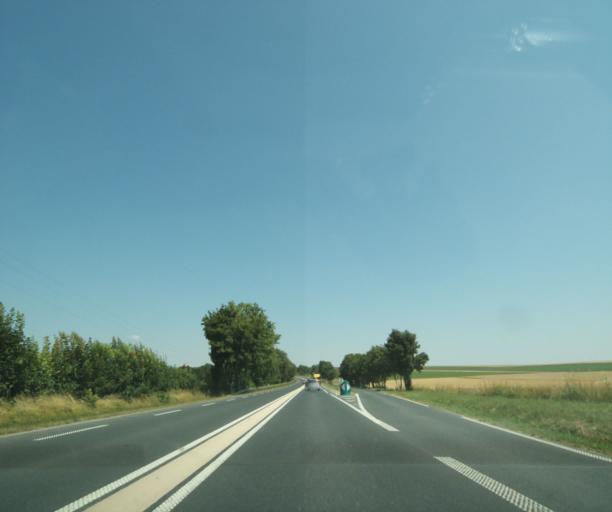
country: FR
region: Champagne-Ardenne
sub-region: Departement de la Marne
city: Mourmelon-le-Grand
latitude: 49.0622
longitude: 4.2971
